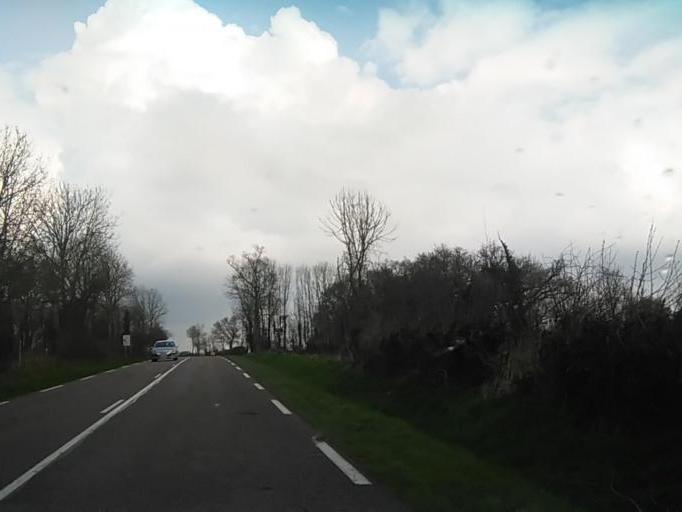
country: FR
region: Lower Normandy
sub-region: Departement de l'Orne
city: Pont-Ecrepin
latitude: 48.7859
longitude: -0.2466
